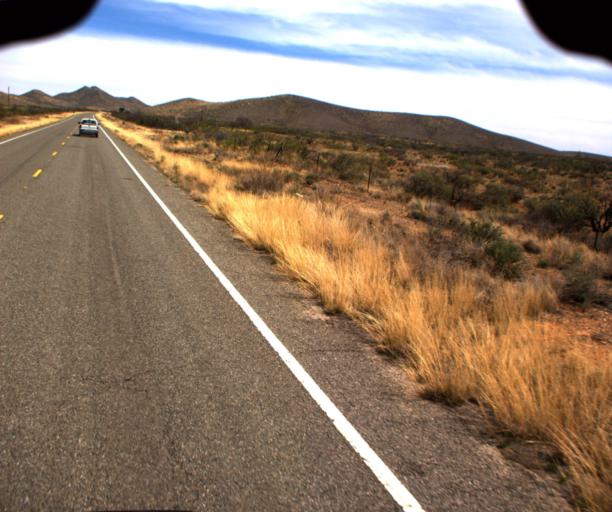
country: US
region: Arizona
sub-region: Cochise County
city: Willcox
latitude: 32.1881
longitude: -109.6835
